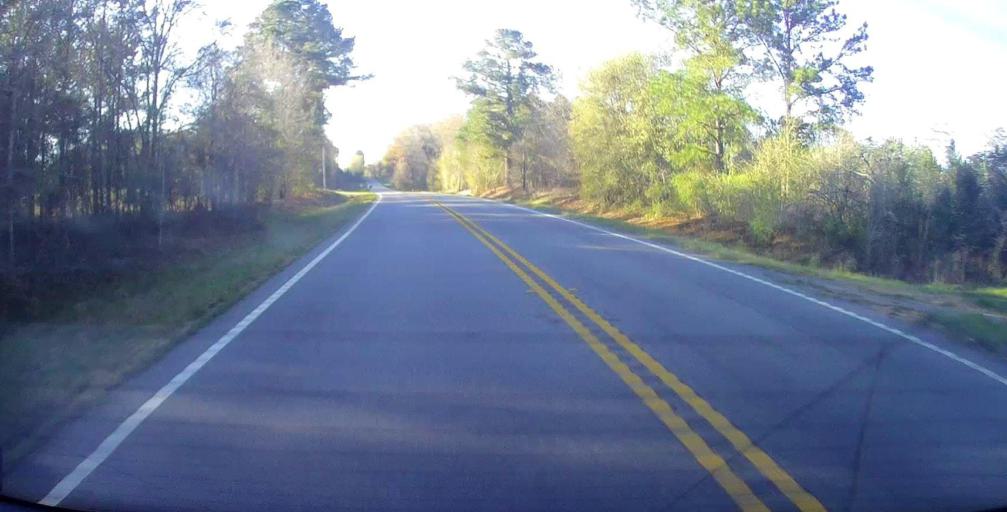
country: US
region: Georgia
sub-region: Pulaski County
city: Hawkinsville
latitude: 32.2361
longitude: -83.3994
